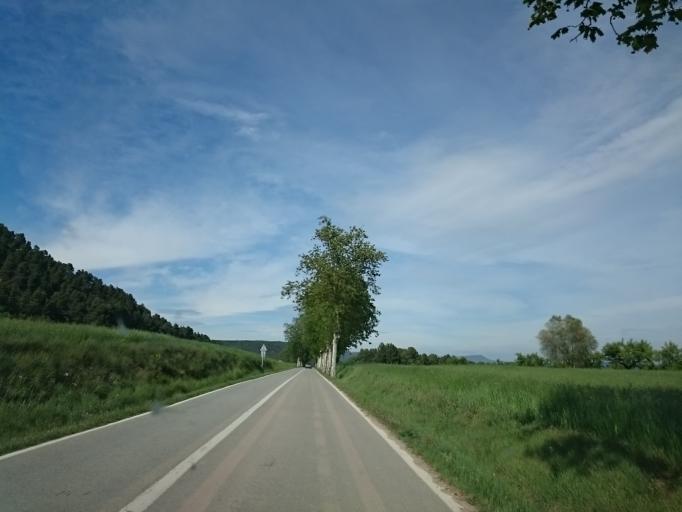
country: ES
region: Catalonia
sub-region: Provincia de Barcelona
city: Sant Marti de Tous
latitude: 41.5670
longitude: 1.5160
